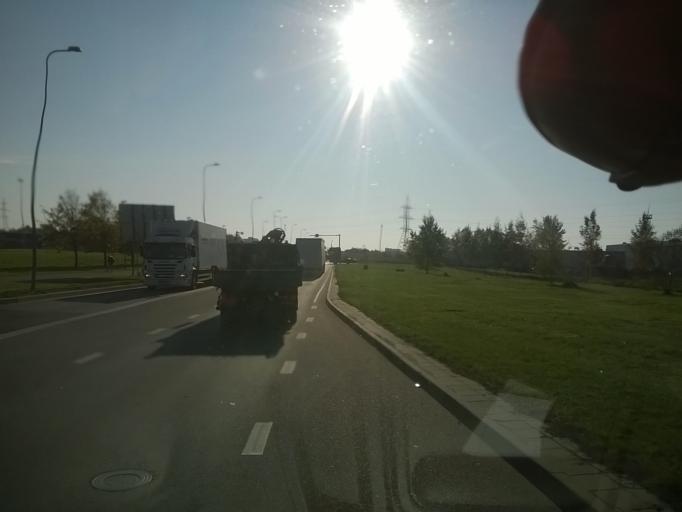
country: EE
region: Harju
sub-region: Tallinna linn
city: Kose
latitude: 59.4266
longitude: 24.8378
